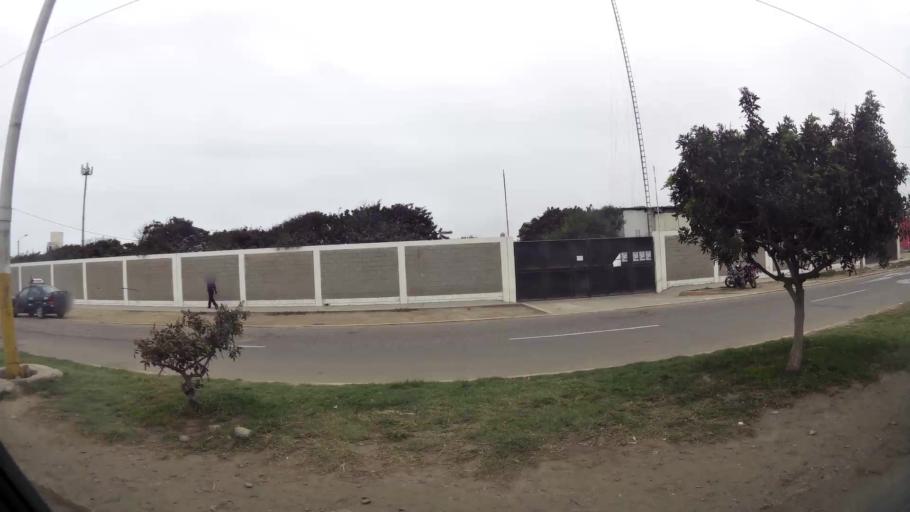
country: PE
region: La Libertad
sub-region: Provincia de Trujillo
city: Buenos Aires
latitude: -8.1401
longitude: -79.0524
